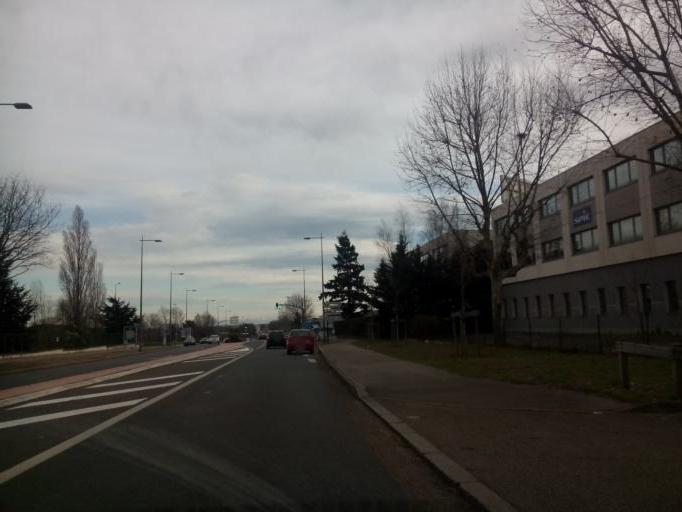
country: FR
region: Rhone-Alpes
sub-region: Departement du Rhone
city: Bron
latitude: 45.7280
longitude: 4.9254
